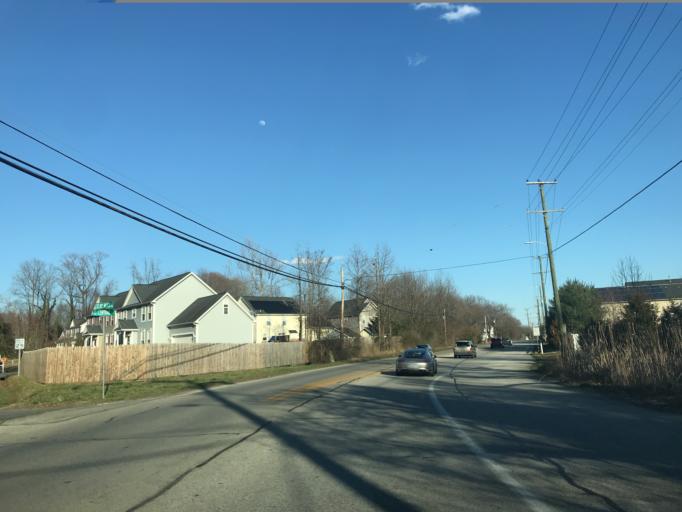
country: US
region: Maryland
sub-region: Anne Arundel County
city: Selby-on-the-Bay
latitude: 38.9061
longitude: -76.5267
